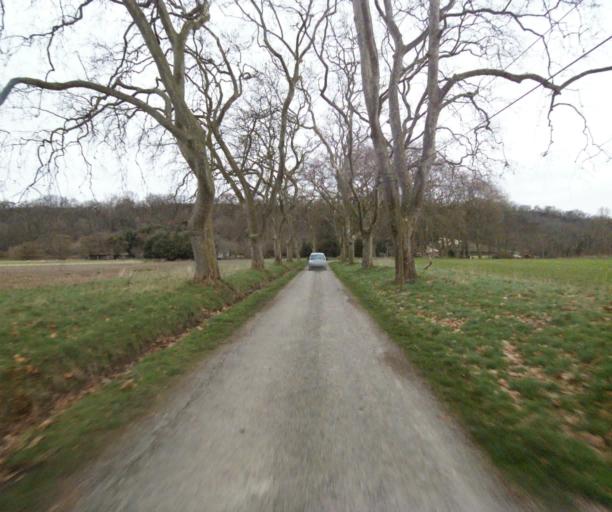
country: FR
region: Midi-Pyrenees
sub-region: Departement de l'Ariege
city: Saverdun
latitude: 43.2198
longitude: 1.5903
